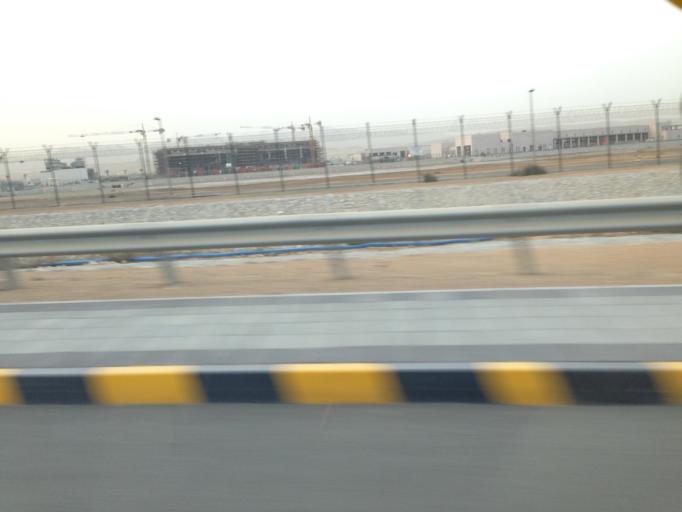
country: OM
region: Muhafazat Masqat
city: Bawshar
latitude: 23.6094
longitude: 58.3066
